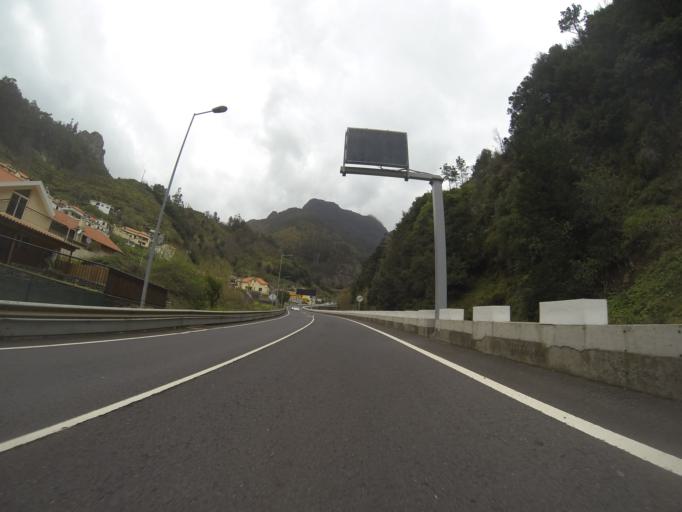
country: PT
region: Madeira
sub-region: Camara de Lobos
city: Curral das Freiras
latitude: 32.7377
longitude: -17.0198
